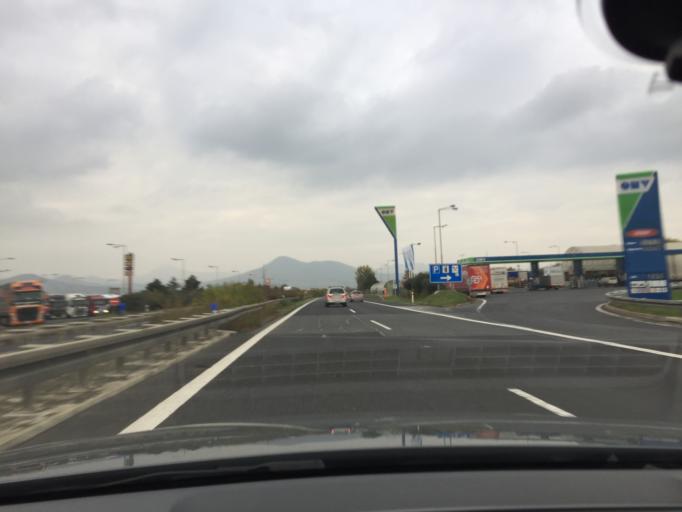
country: CZ
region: Ustecky
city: Lovosice
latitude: 50.4792
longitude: 14.0849
